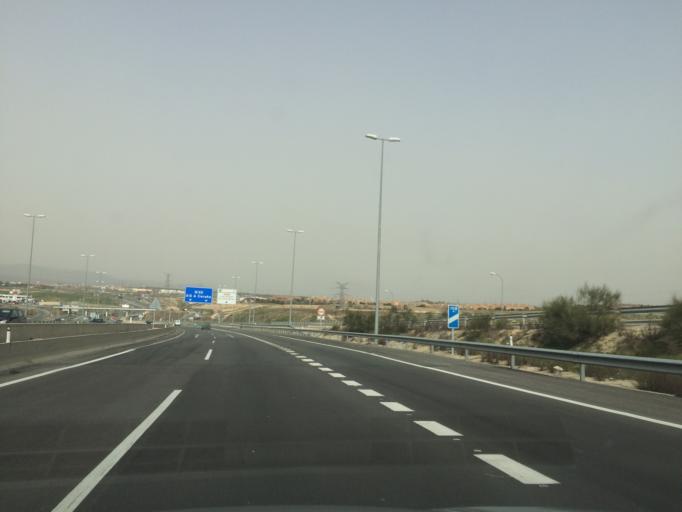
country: ES
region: Madrid
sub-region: Provincia de Madrid
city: Las Rozas de Madrid
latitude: 40.4810
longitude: -3.8957
